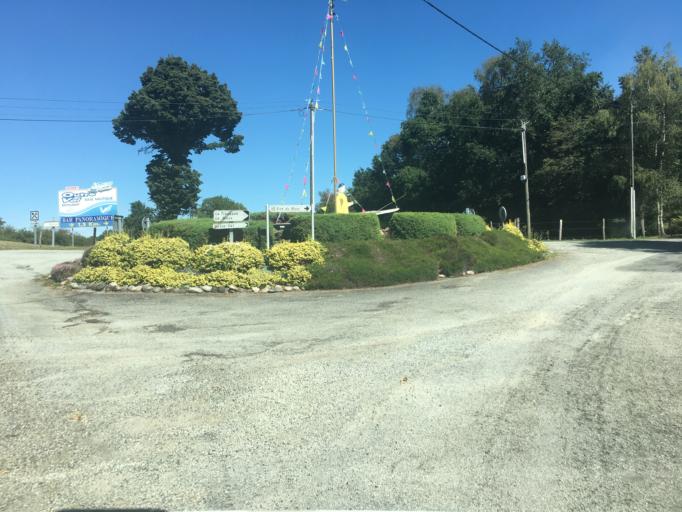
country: FR
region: Limousin
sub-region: Departement de la Correze
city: Bort-les-Orgues
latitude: 45.4439
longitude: 2.4815
